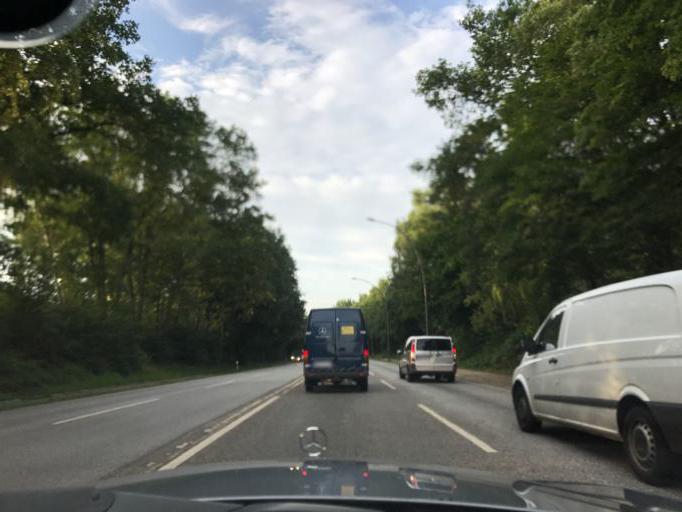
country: DE
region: Schleswig-Holstein
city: Glinde
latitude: 53.5051
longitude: 10.1844
